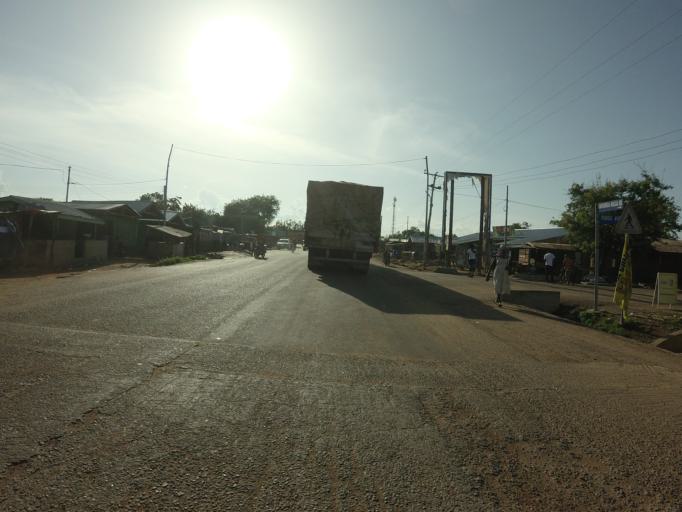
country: GH
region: Upper East
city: Navrongo
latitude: 10.8958
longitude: -1.0849
